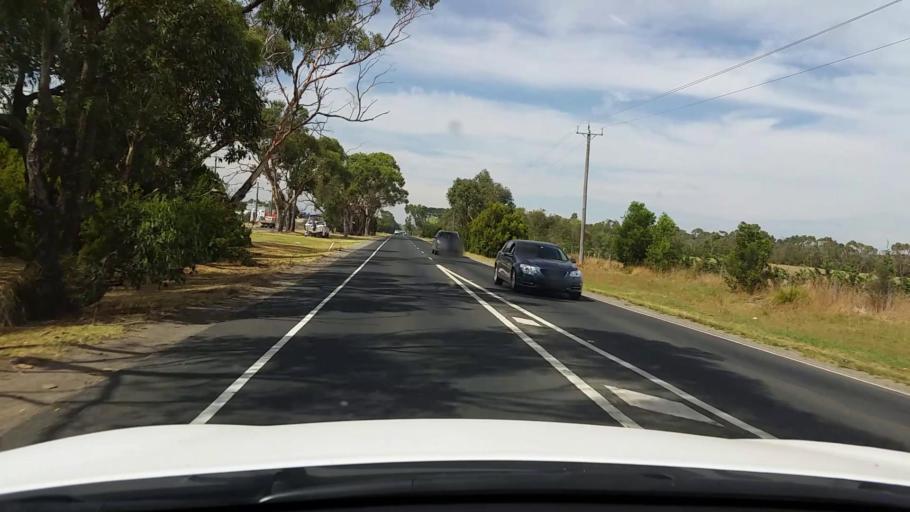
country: AU
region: Victoria
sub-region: Mornington Peninsula
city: Hastings
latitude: -38.2875
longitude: 145.1836
